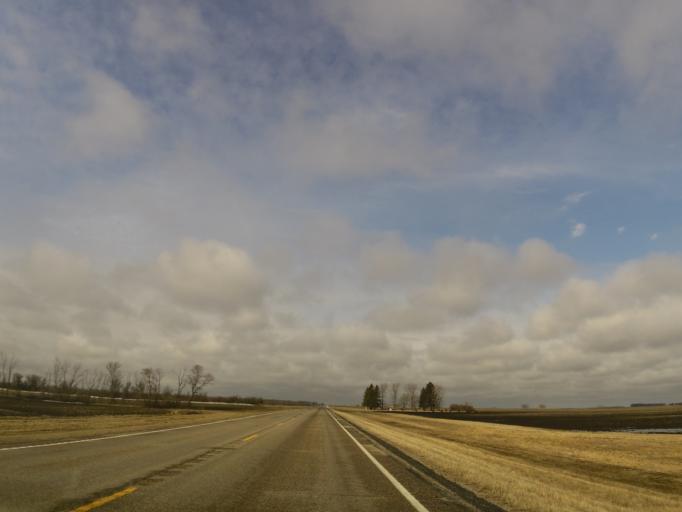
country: US
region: North Dakota
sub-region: Traill County
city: Hillsboro
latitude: 47.4978
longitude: -97.1412
